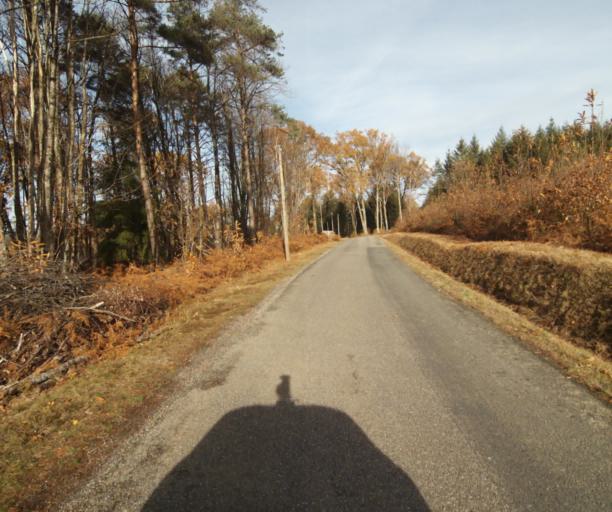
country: FR
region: Limousin
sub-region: Departement de la Correze
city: Sainte-Fortunade
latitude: 45.1874
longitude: 1.7388
